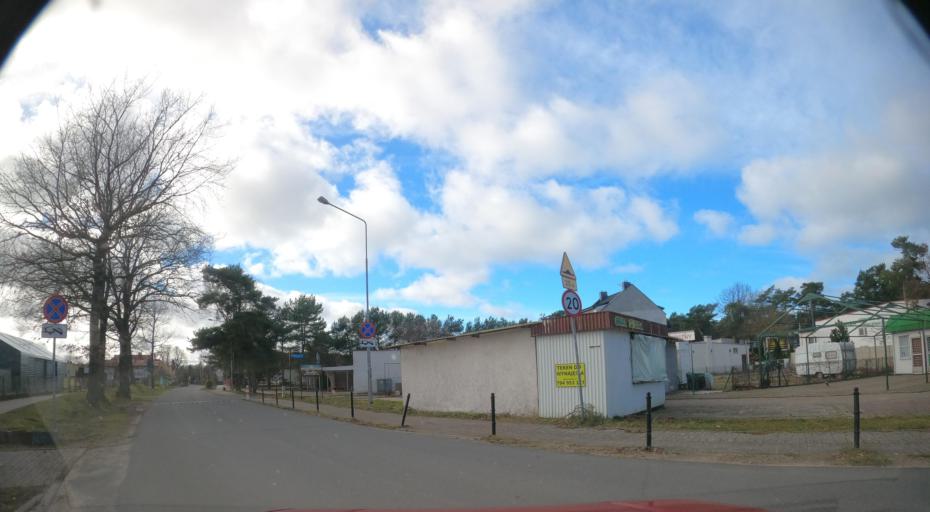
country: PL
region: West Pomeranian Voivodeship
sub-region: Koszalin
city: Koszalin
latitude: 54.3088
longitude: 16.1994
